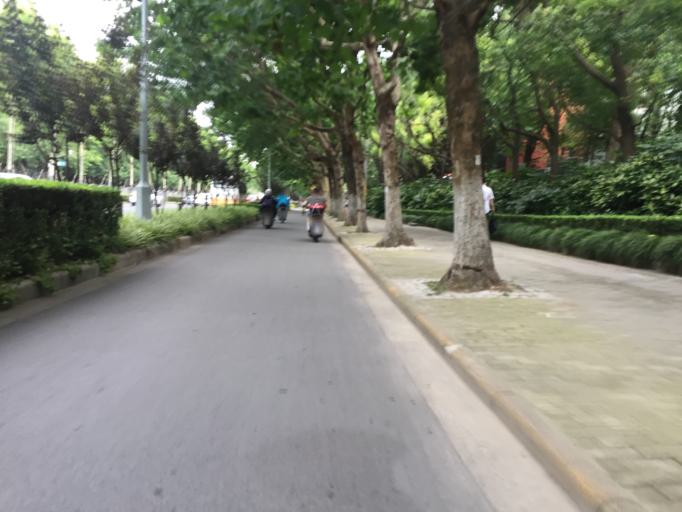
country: CN
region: Shanghai Shi
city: Huamu
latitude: 31.1854
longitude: 121.5367
